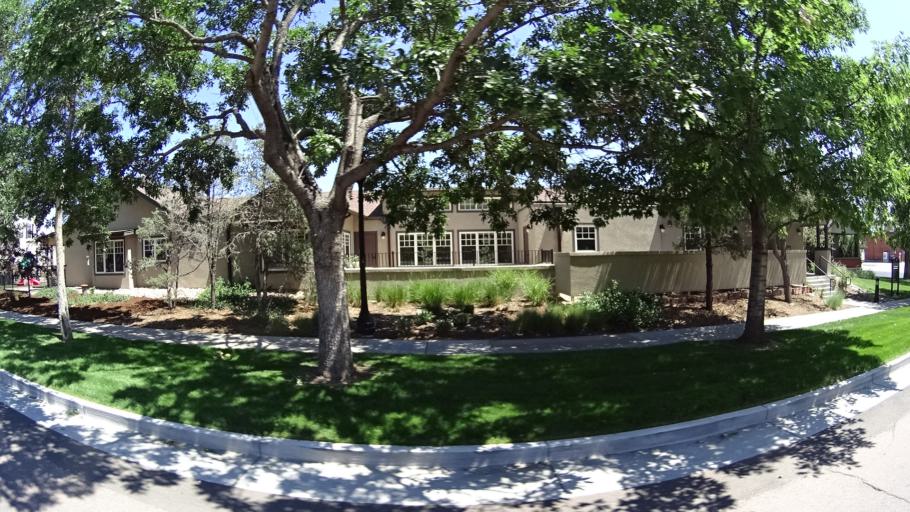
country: US
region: Colorado
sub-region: El Paso County
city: Colorado Springs
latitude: 38.8468
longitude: -104.8209
